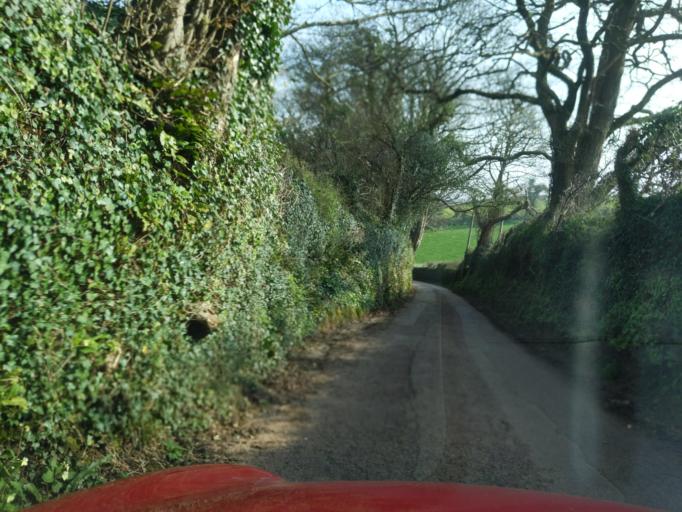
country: GB
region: England
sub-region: Devon
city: Kingsbridge
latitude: 50.2865
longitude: -3.7263
